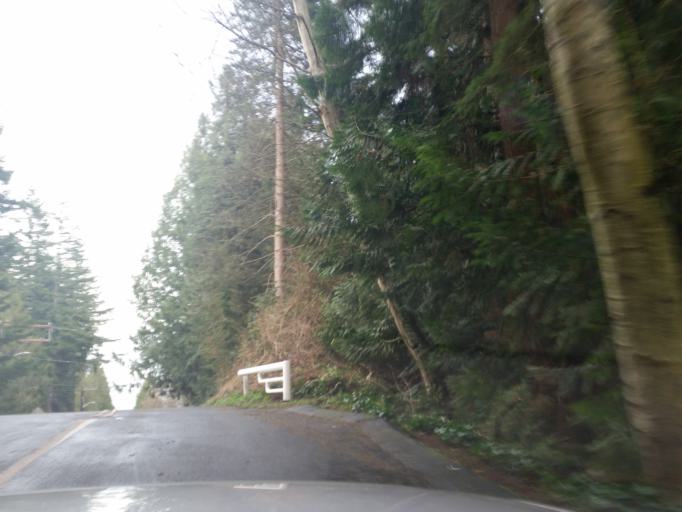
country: US
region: Washington
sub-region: Snohomish County
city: Meadowdale
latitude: 47.8574
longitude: -122.3155
